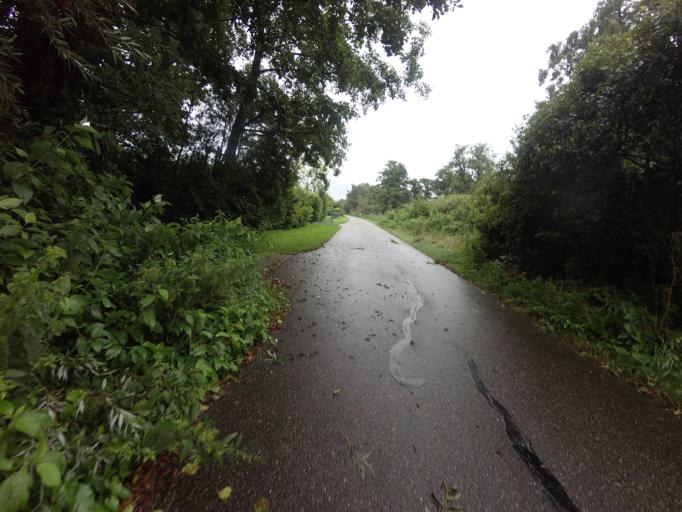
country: NL
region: Overijssel
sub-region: Gemeente Steenwijkerland
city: Blokzijl
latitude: 52.7696
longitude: 5.9863
